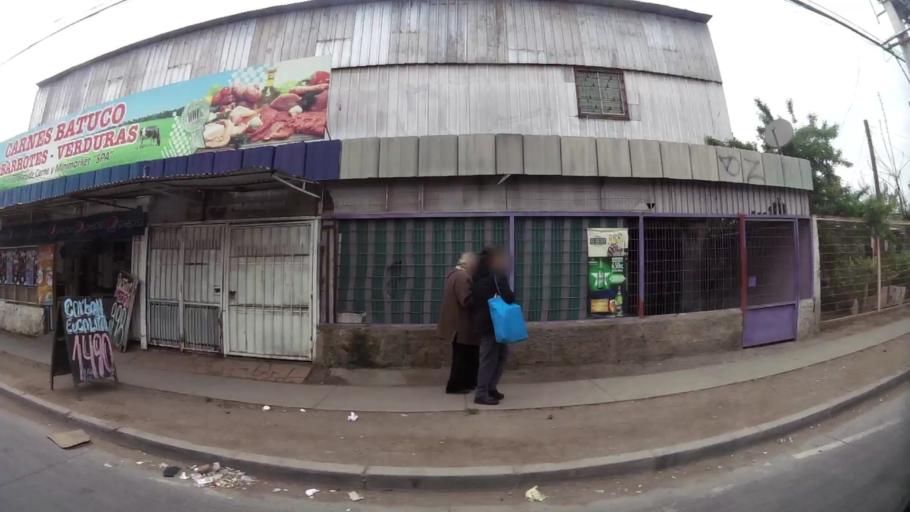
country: CL
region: Santiago Metropolitan
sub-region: Provincia de Chacabuco
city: Lampa
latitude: -33.2325
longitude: -70.8073
